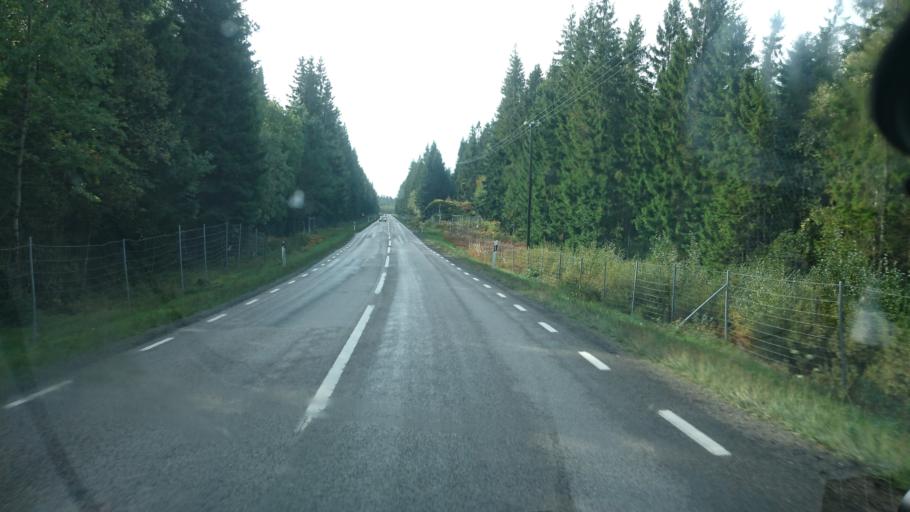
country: SE
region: Vaestra Goetaland
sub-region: Alingsas Kommun
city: Sollebrunn
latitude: 58.1878
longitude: 12.4261
